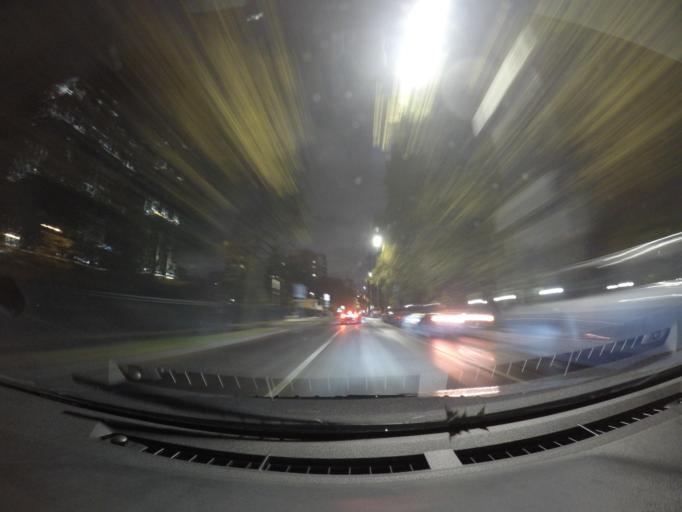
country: RU
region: Moscow
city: Likhobory
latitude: 55.8215
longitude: 37.5702
